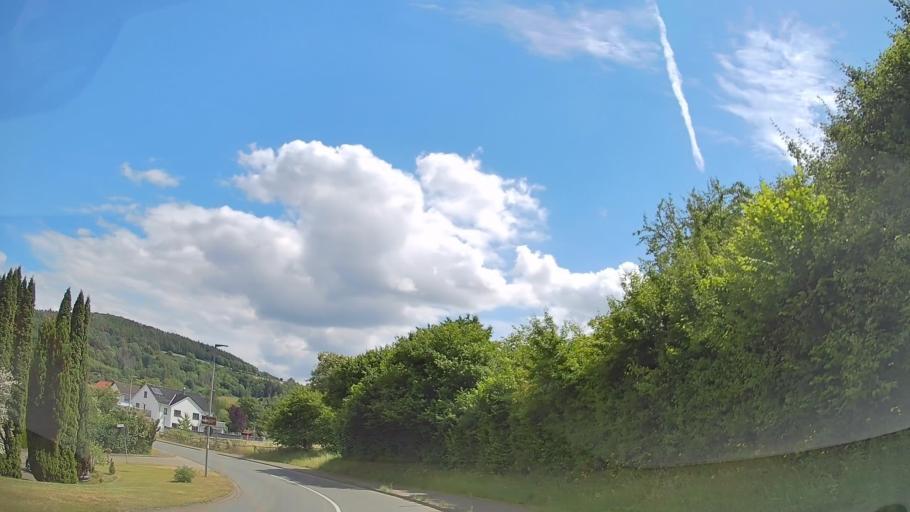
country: DE
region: North Rhine-Westphalia
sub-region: Regierungsbezirk Detmold
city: Lugde
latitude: 51.9591
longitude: 9.2400
